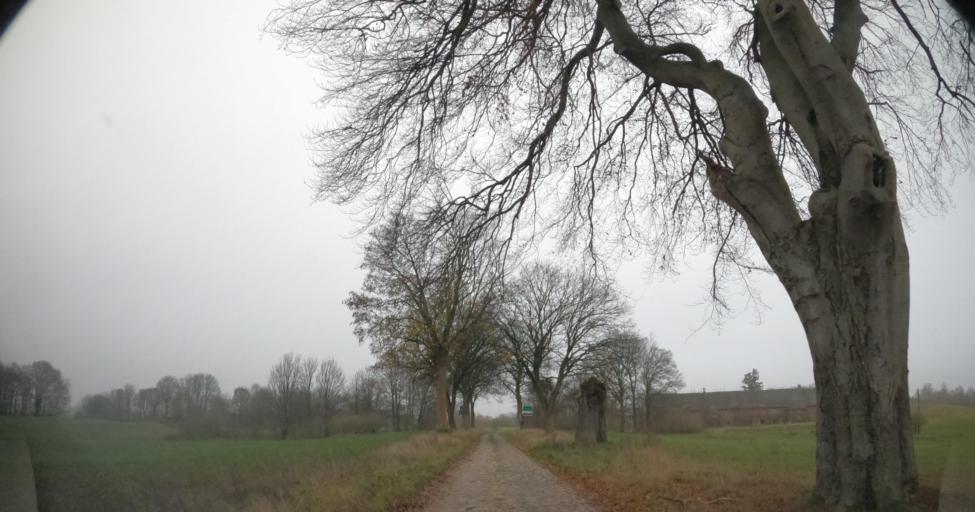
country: PL
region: West Pomeranian Voivodeship
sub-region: Powiat drawski
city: Drawsko Pomorskie
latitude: 53.5425
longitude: 15.7285
